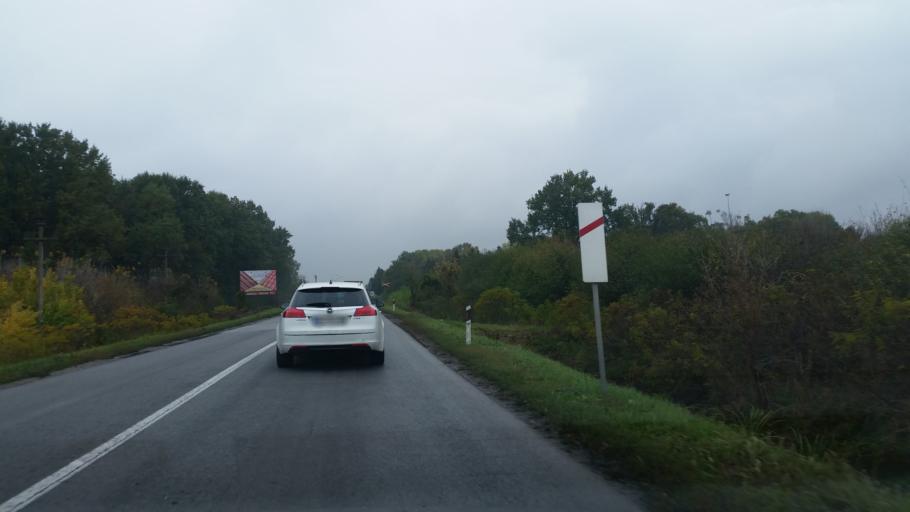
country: RS
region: Central Serbia
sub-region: Belgrade
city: Zemun
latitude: 44.9253
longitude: 20.4363
